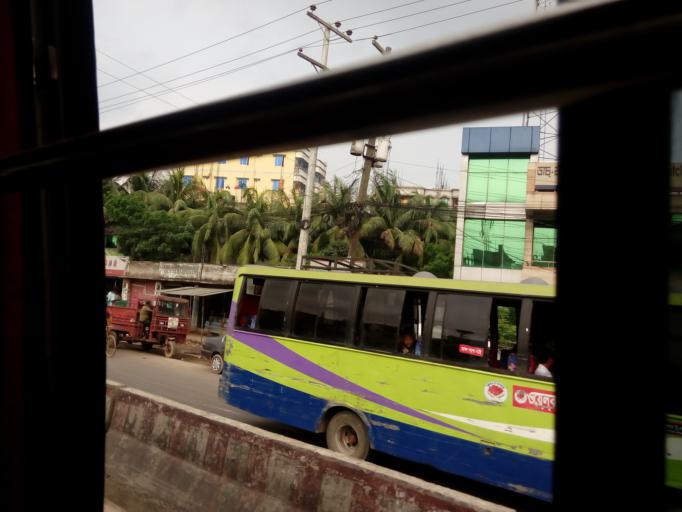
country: BD
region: Dhaka
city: Tungi
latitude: 23.9429
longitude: 90.2720
